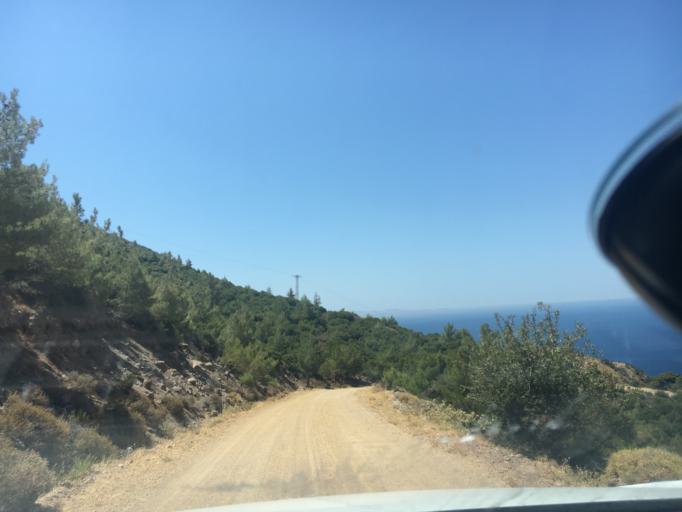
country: TR
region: Canakkale
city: Gulpinar
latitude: 39.4821
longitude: 26.0745
